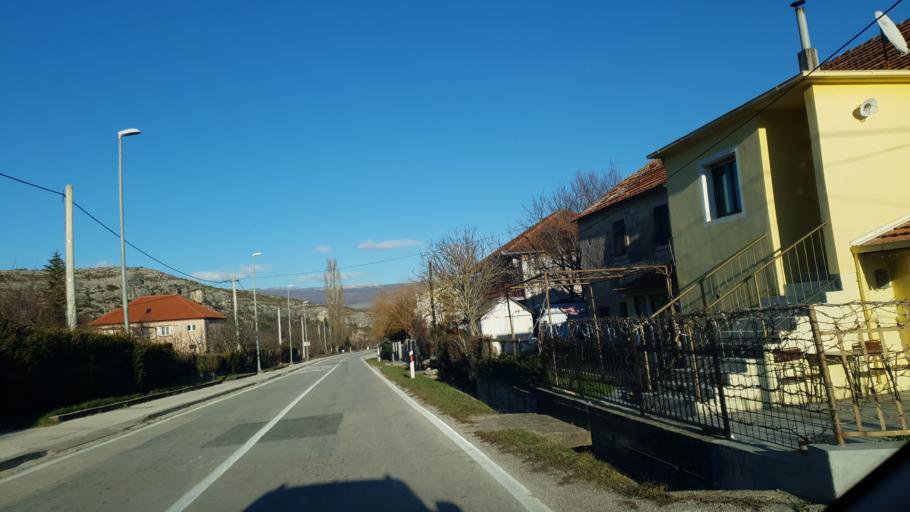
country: HR
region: Splitsko-Dalmatinska
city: Sinj
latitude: 43.7152
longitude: 16.6633
